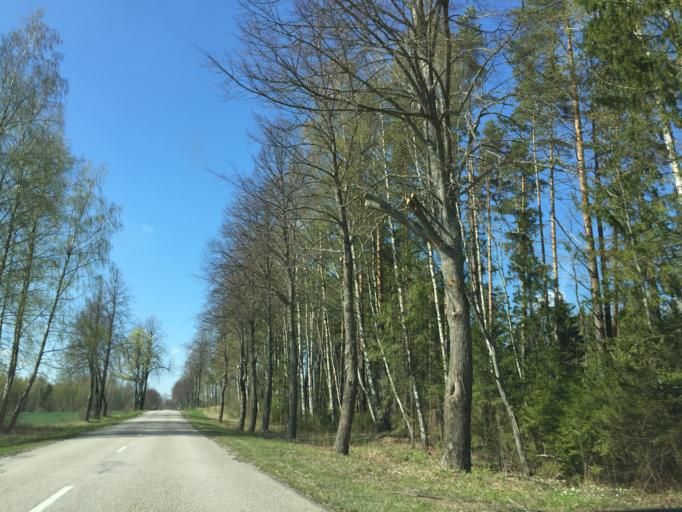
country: LV
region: Strenci
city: Seda
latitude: 57.5730
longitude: 25.7950
